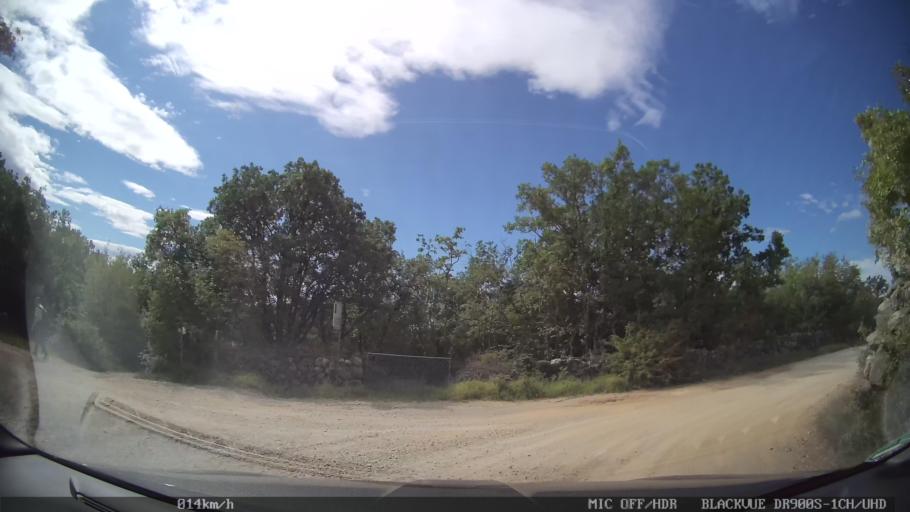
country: HR
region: Primorsko-Goranska
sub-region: Grad Krk
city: Krk
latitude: 45.0367
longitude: 14.5342
